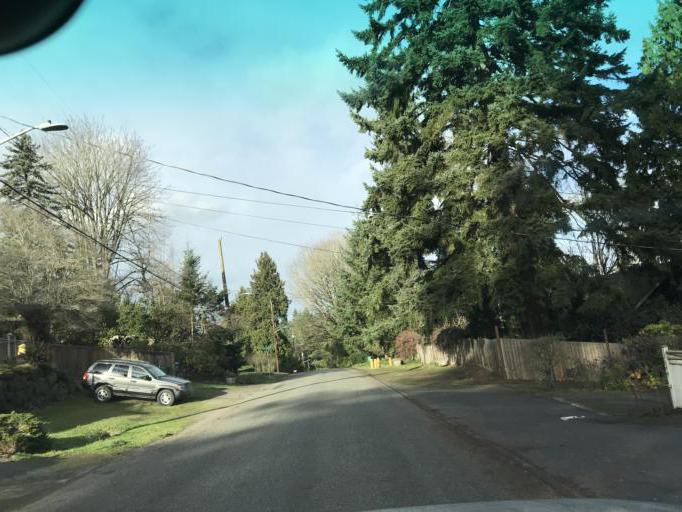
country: US
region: Washington
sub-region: King County
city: Lake Forest Park
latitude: 47.7170
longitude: -122.3045
